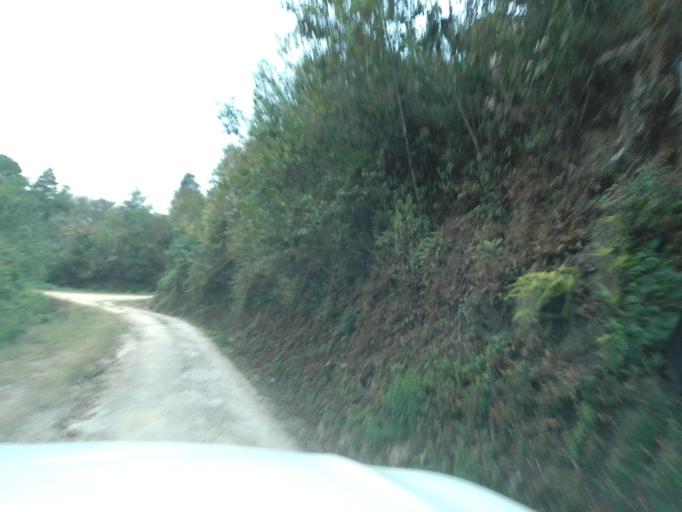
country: MX
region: Chiapas
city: Motozintla de Mendoza
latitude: 15.2100
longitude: -92.2248
